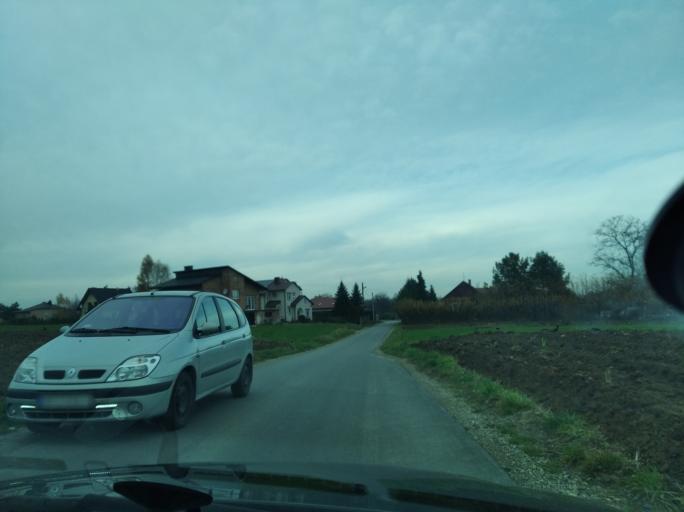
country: PL
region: Subcarpathian Voivodeship
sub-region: Powiat przeworski
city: Grzeska
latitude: 50.0729
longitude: 22.4566
